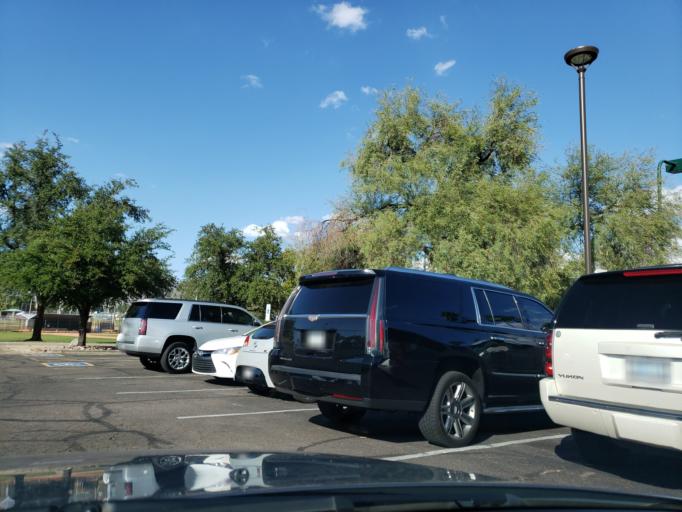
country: US
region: Arizona
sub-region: Maricopa County
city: Scottsdale
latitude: 33.5754
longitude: -111.8584
